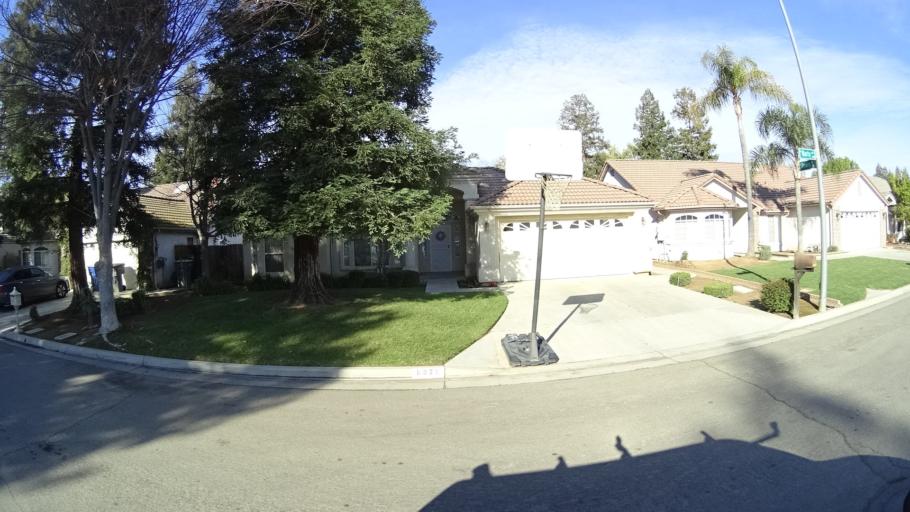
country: US
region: California
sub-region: Fresno County
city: Fresno
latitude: 36.8285
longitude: -119.8581
